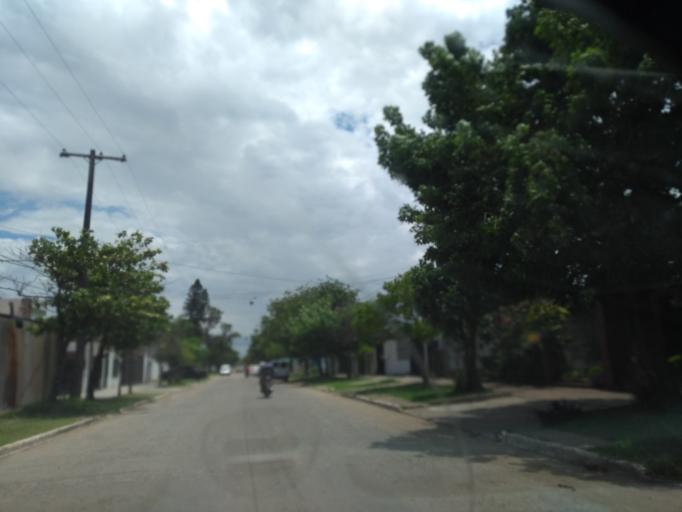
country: AR
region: Chaco
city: Resistencia
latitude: -27.4708
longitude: -58.9626
